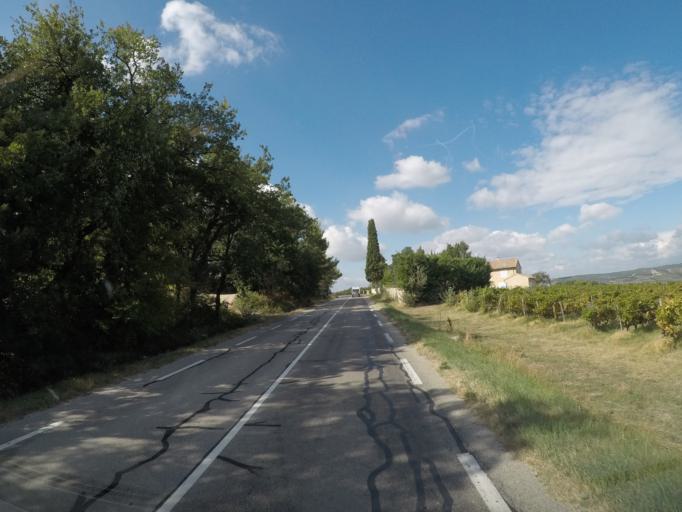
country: FR
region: Provence-Alpes-Cote d'Azur
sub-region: Departement du Vaucluse
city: Vaison-la-Romaine
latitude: 44.2727
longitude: 5.0143
